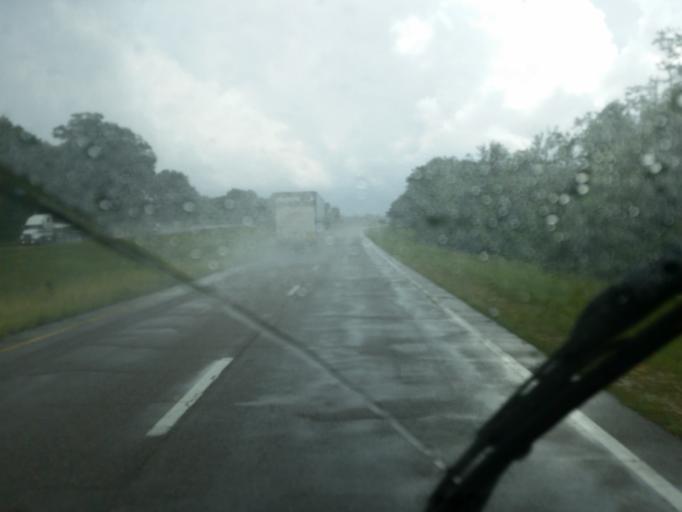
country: US
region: Mississippi
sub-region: George County
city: Lucedale
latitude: 30.9011
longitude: -88.4624
